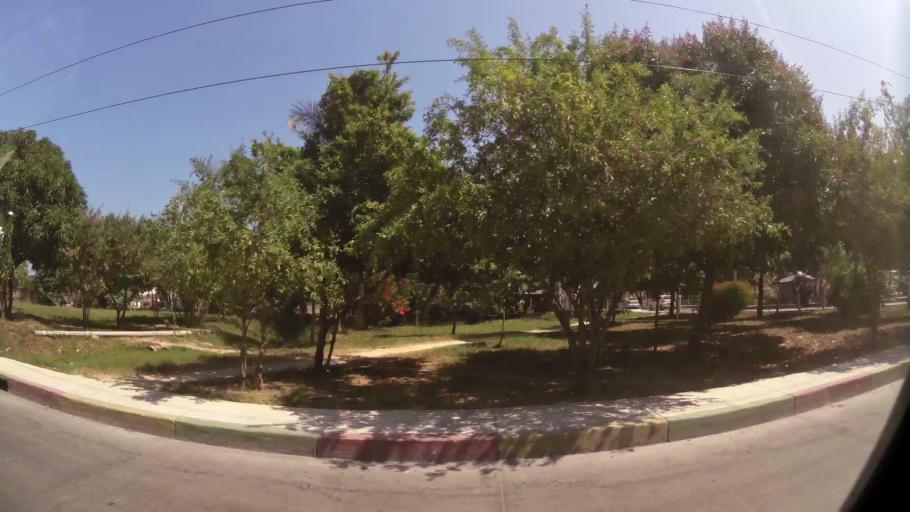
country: CO
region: Bolivar
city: Cartagena
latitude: 10.3990
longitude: -75.4862
